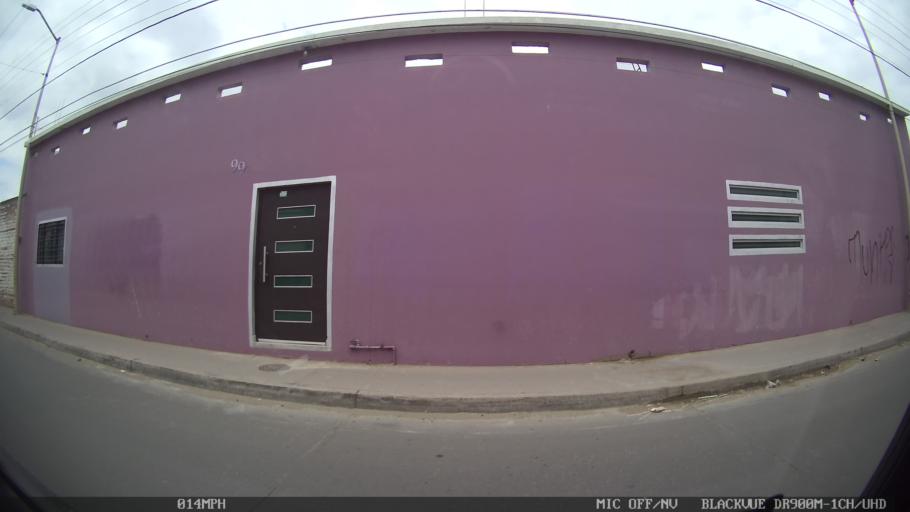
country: MX
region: Jalisco
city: Tonala
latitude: 20.6500
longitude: -103.2531
